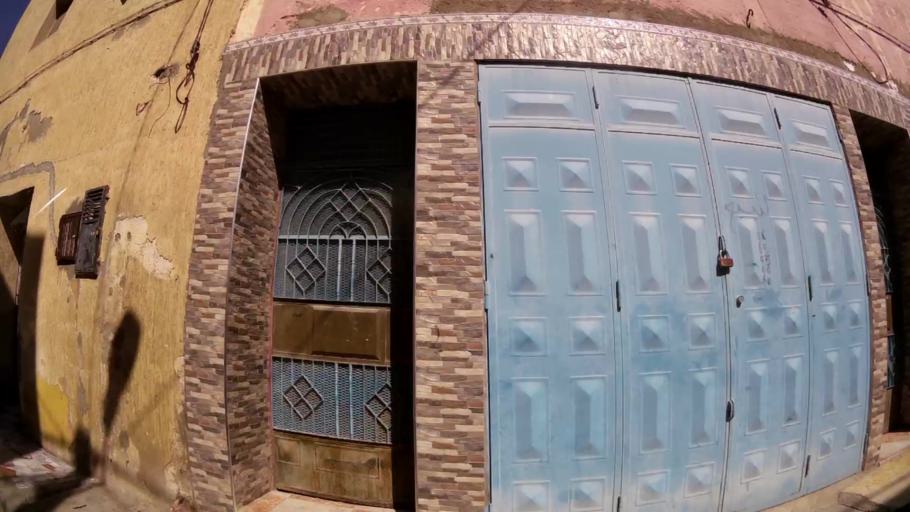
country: MA
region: Oriental
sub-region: Oujda-Angad
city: Oujda
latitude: 34.6841
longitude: -1.9281
